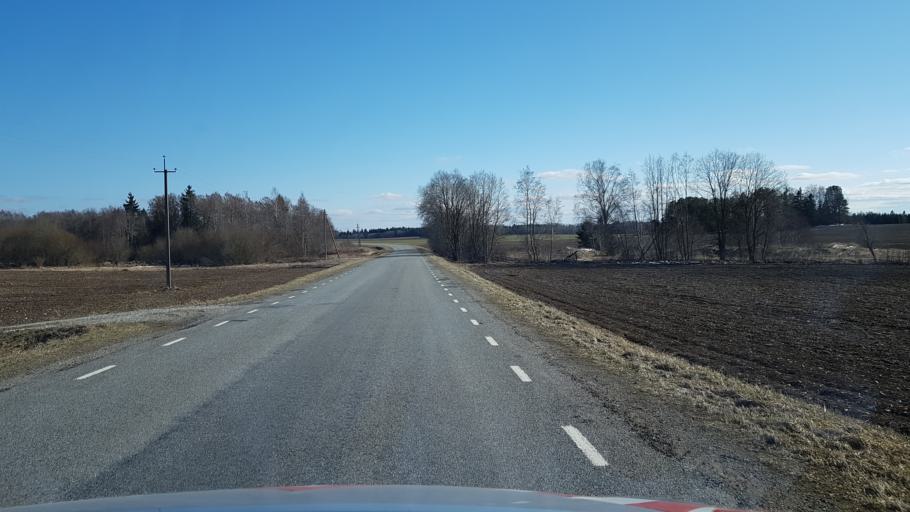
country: EE
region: Laeaene-Virumaa
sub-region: Kadrina vald
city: Kadrina
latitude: 59.3693
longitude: 26.0474
